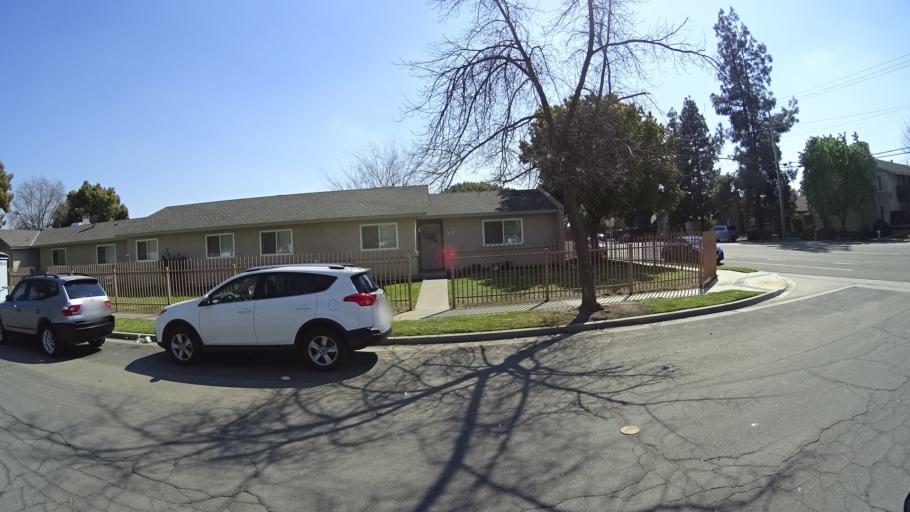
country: US
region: California
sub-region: Fresno County
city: Tarpey Village
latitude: 36.7959
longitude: -119.7360
